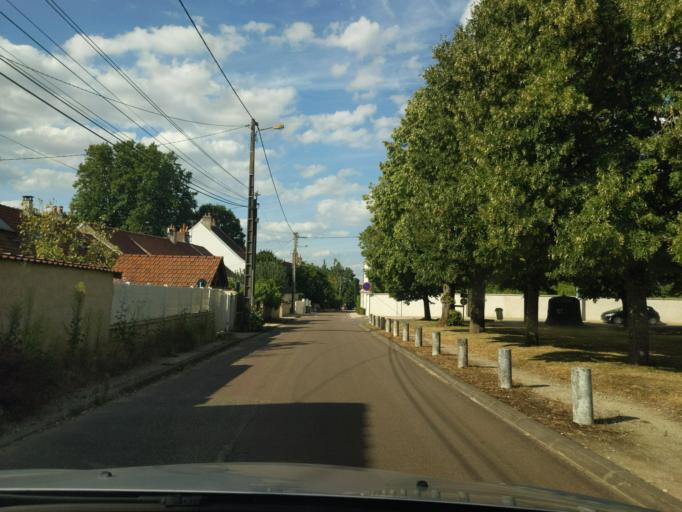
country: FR
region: Bourgogne
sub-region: Departement de la Cote-d'Or
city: Ruffey-les-Echirey
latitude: 47.3997
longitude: 5.0858
